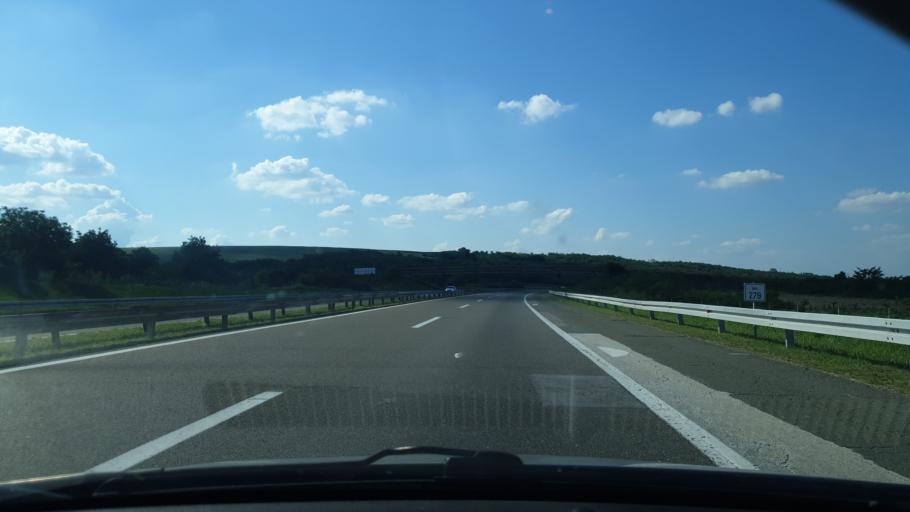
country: RS
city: Lugavcina
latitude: 44.4573
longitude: 21.0417
